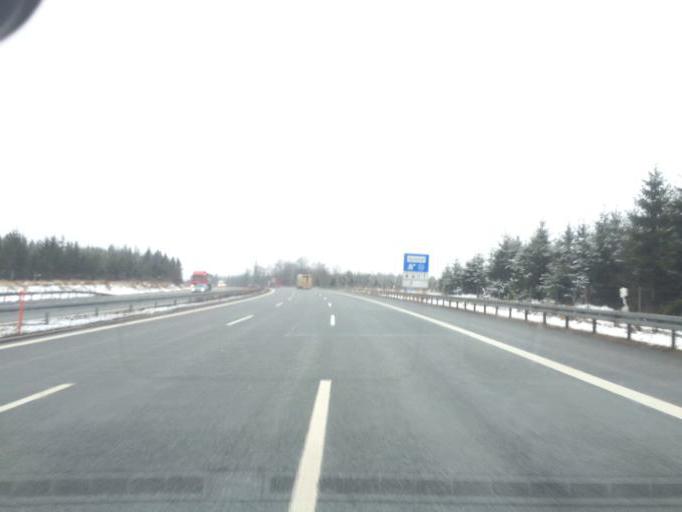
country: DE
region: Bavaria
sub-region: Upper Franconia
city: Berg
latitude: 50.3567
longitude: 11.7810
